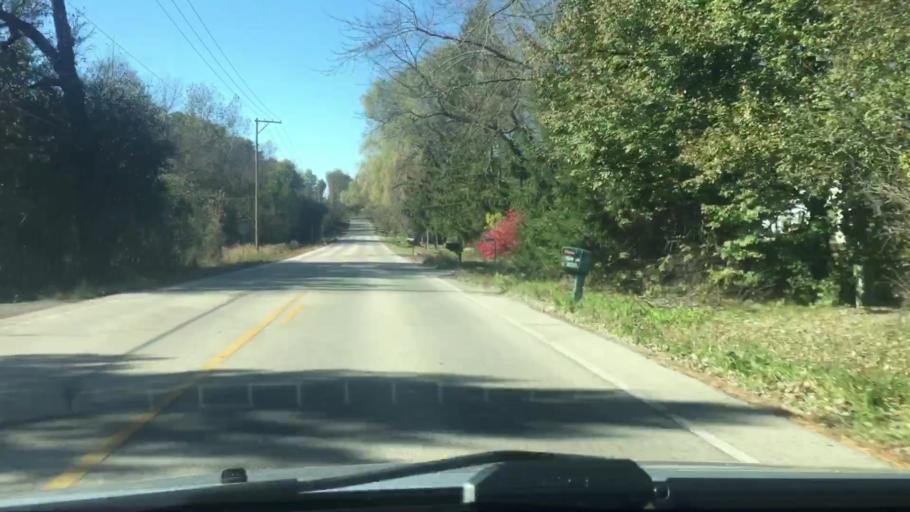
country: US
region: Wisconsin
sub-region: Waukesha County
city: Wales
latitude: 42.9882
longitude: -88.3485
